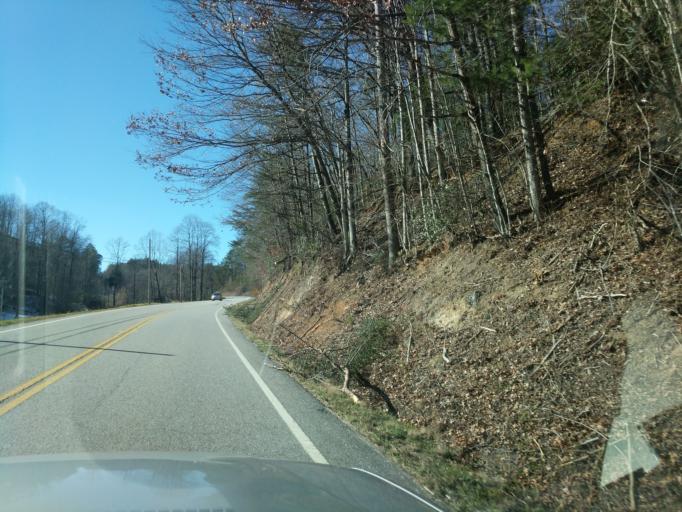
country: US
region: Georgia
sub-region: Rabun County
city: Clayton
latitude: 34.8754
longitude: -83.4493
